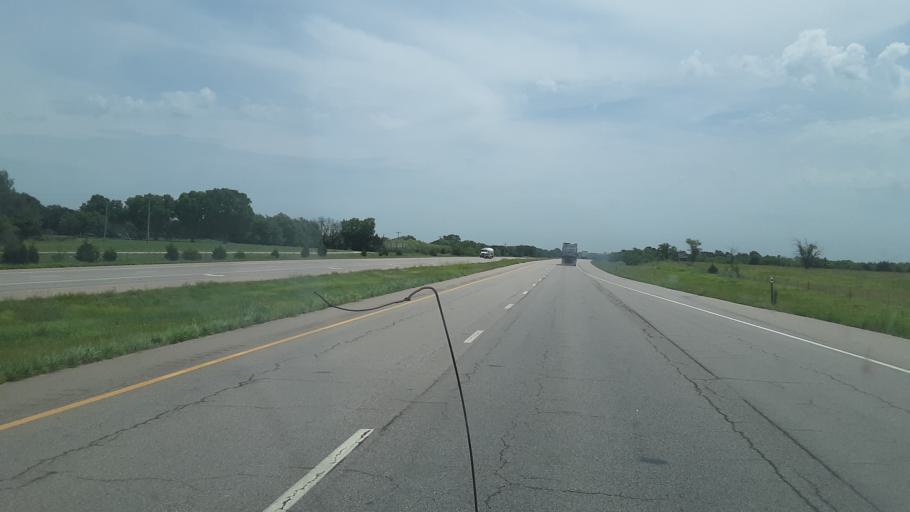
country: US
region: Kansas
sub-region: Butler County
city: Towanda
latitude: 37.7957
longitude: -97.0343
